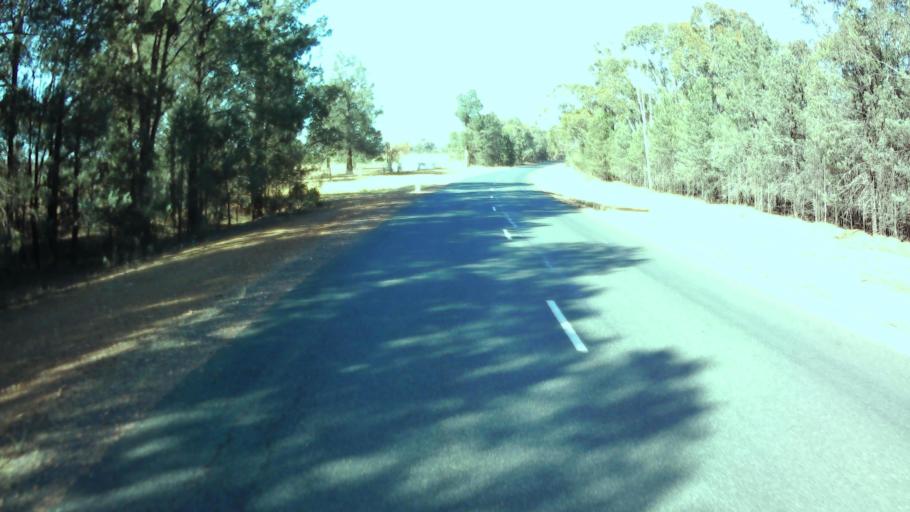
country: AU
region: New South Wales
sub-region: Weddin
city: Grenfell
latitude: -34.0335
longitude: 148.0895
